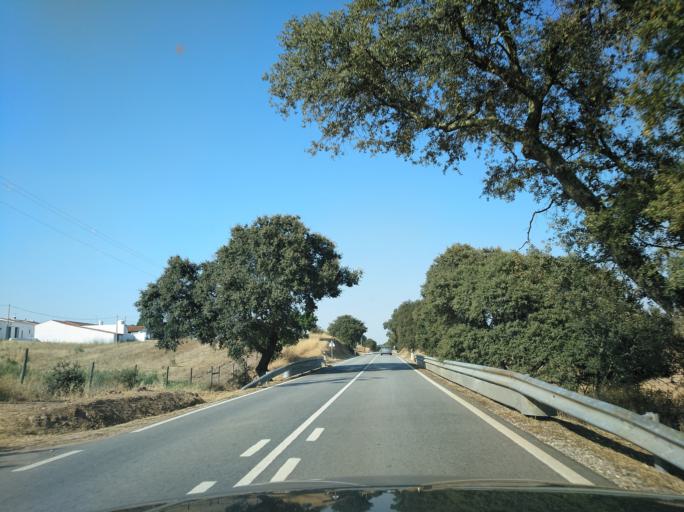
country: ES
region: Andalusia
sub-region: Provincia de Huelva
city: Rosal de la Frontera
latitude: 37.9894
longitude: -7.2921
